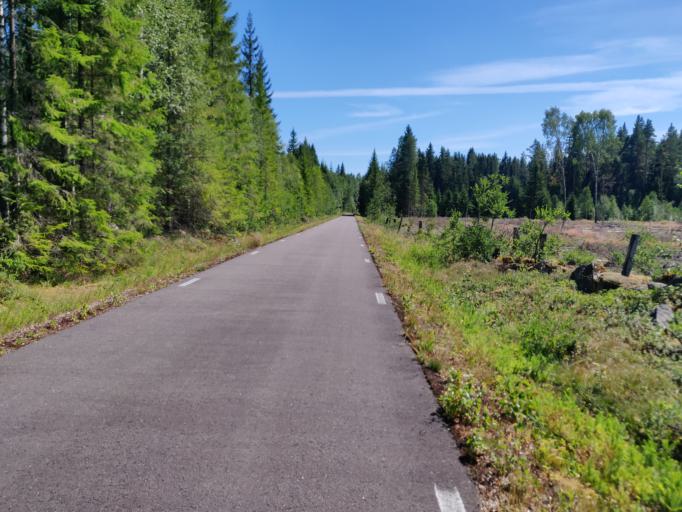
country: SE
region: Vaermland
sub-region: Munkfors Kommun
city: Munkfors
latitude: 59.9418
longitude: 13.5874
